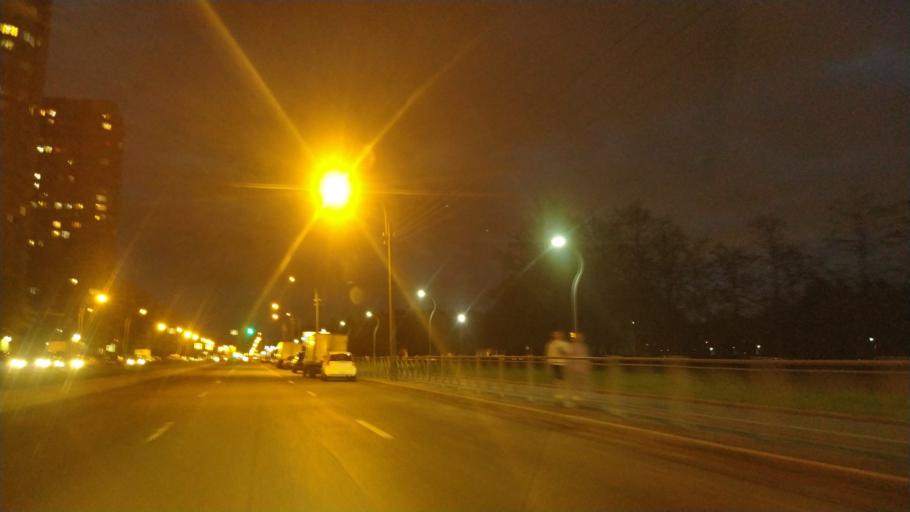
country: RU
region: St.-Petersburg
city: Sosnovka
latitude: 60.0354
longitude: 30.3699
